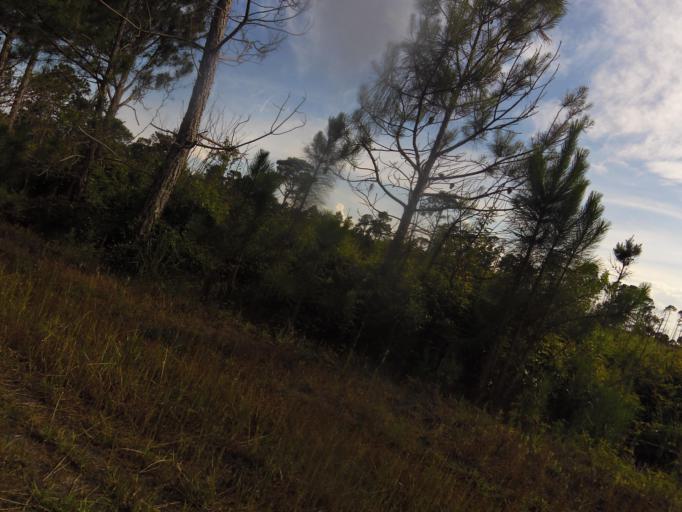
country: US
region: Florida
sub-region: Saint Johns County
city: Villano Beach
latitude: 30.0267
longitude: -81.3432
